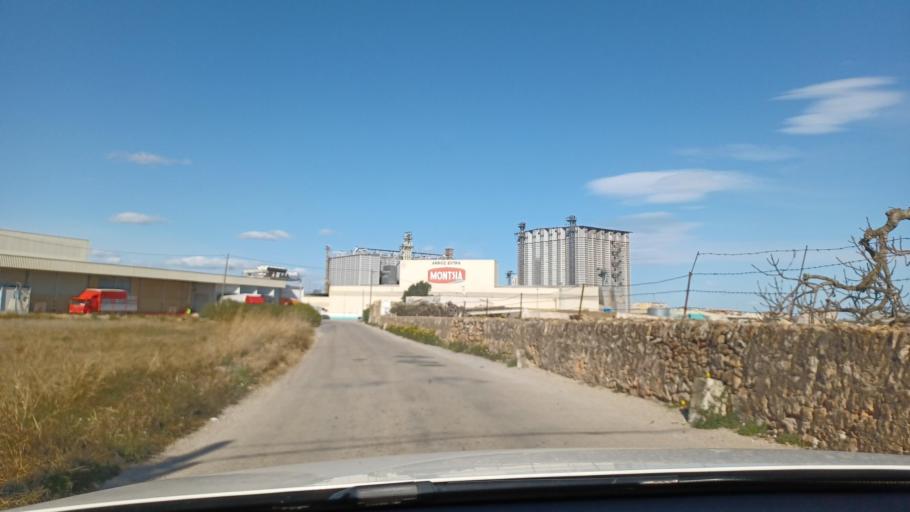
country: ES
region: Catalonia
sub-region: Provincia de Tarragona
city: Amposta
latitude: 40.6985
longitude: 0.5759
